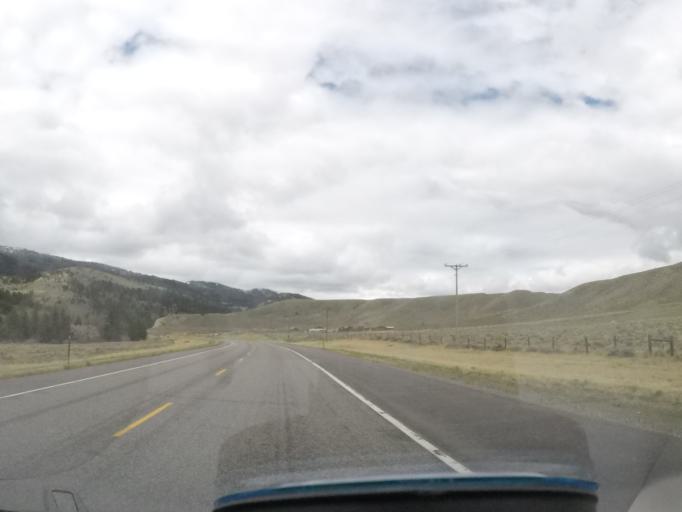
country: US
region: Wyoming
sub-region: Sublette County
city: Pinedale
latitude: 43.5789
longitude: -109.7448
